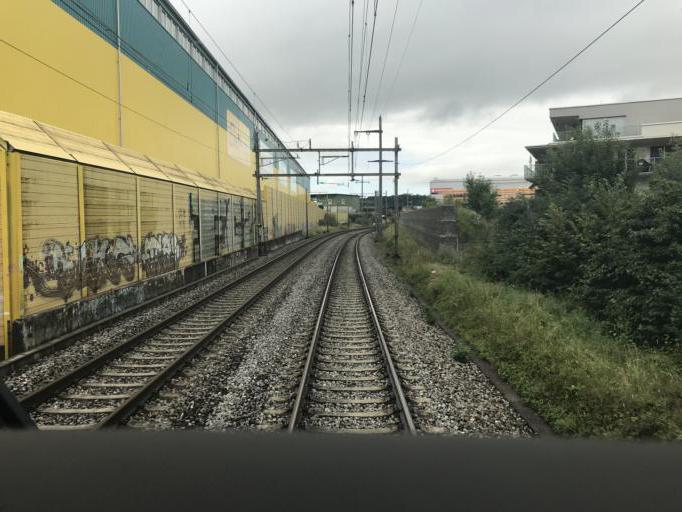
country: CH
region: Zurich
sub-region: Bezirk Dielsdorf
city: Hofstetten
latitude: 47.4783
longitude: 8.5025
